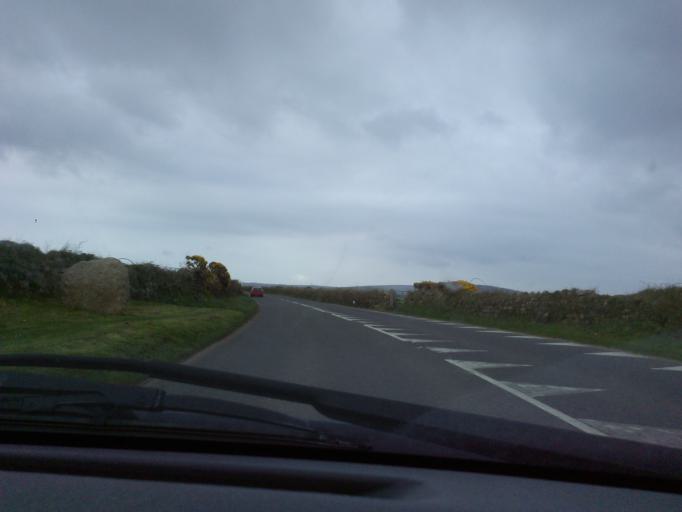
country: GB
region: England
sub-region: Cornwall
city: Sennen
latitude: 50.0802
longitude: -5.6817
